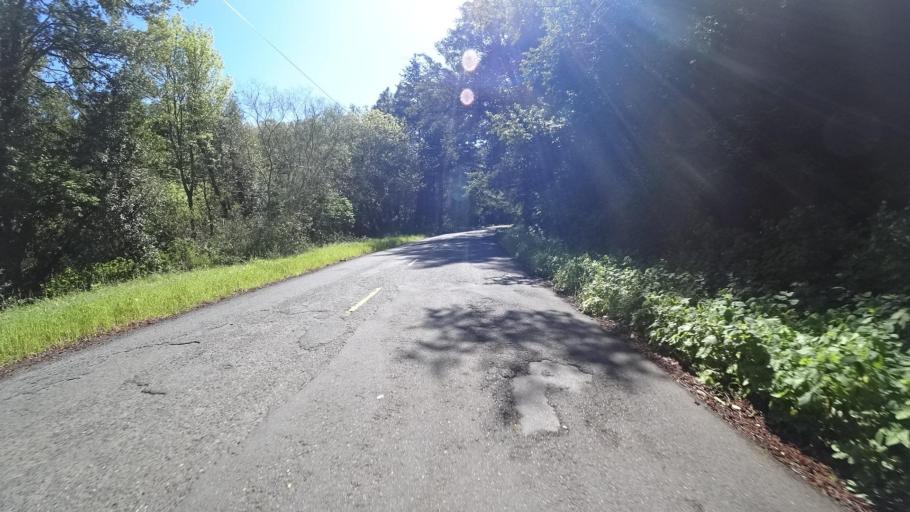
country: US
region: California
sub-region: Humboldt County
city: Rio Dell
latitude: 40.3110
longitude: -124.2636
